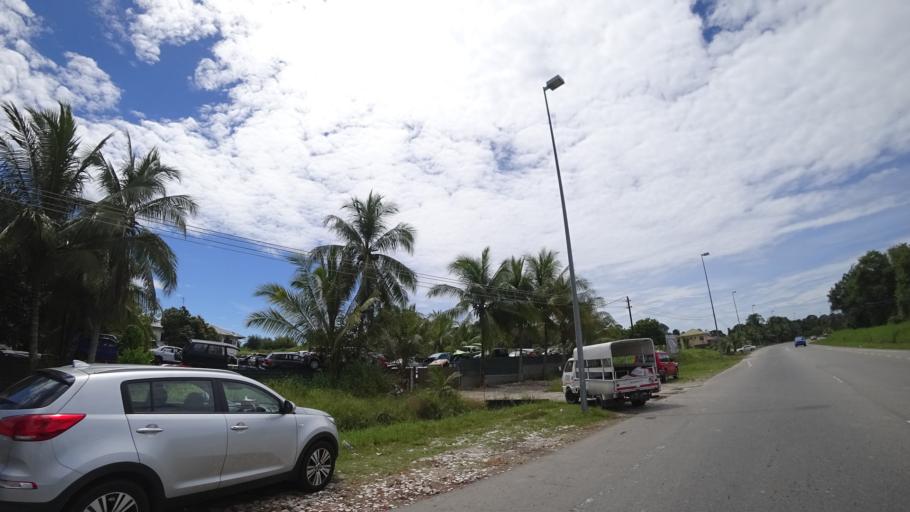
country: BN
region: Brunei and Muara
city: Bandar Seri Begawan
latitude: 4.8174
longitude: 114.8405
